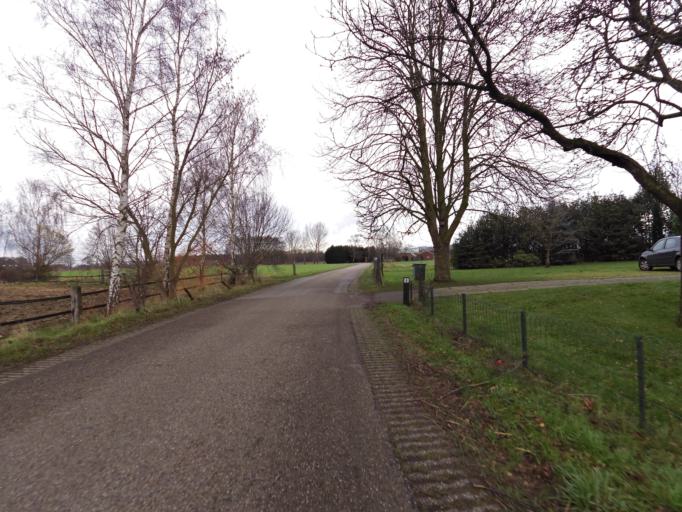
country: NL
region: Gelderland
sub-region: Oude IJsselstreek
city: Wisch
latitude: 51.9173
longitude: 6.3878
